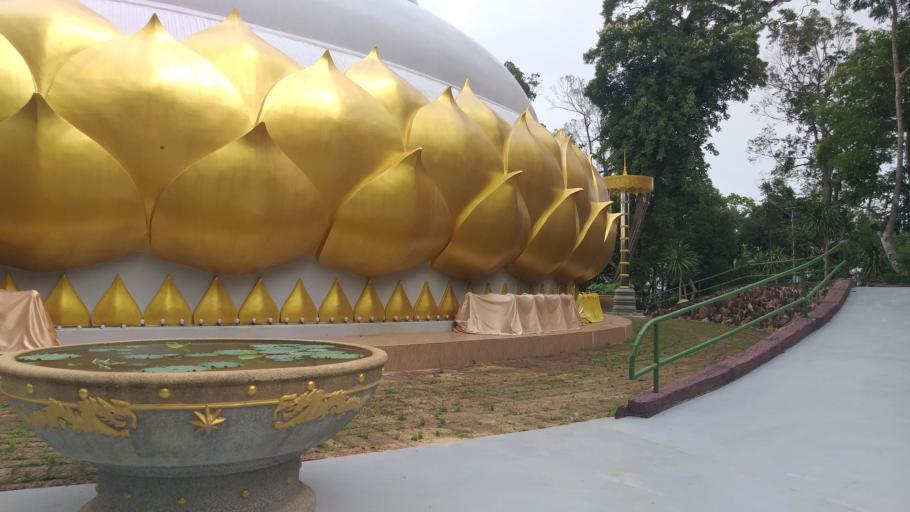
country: TH
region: Nakhon Ratchasima
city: Sikhio
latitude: 14.6847
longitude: 101.6915
